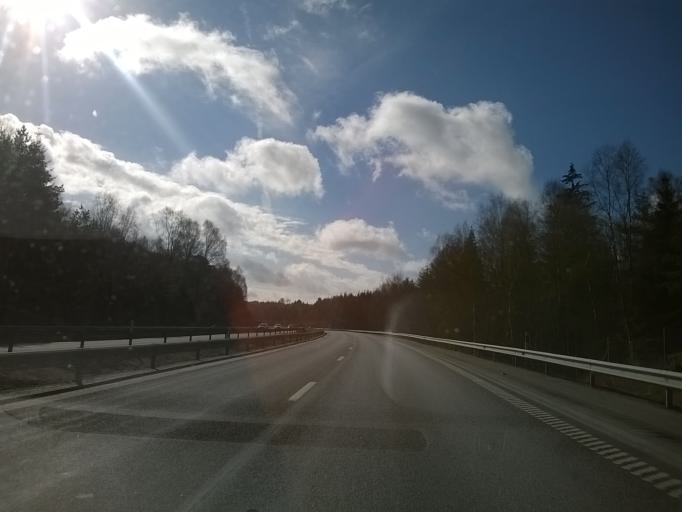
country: SE
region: Halland
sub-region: Kungsbacka Kommun
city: Kungsbacka
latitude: 57.4793
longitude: 12.0436
